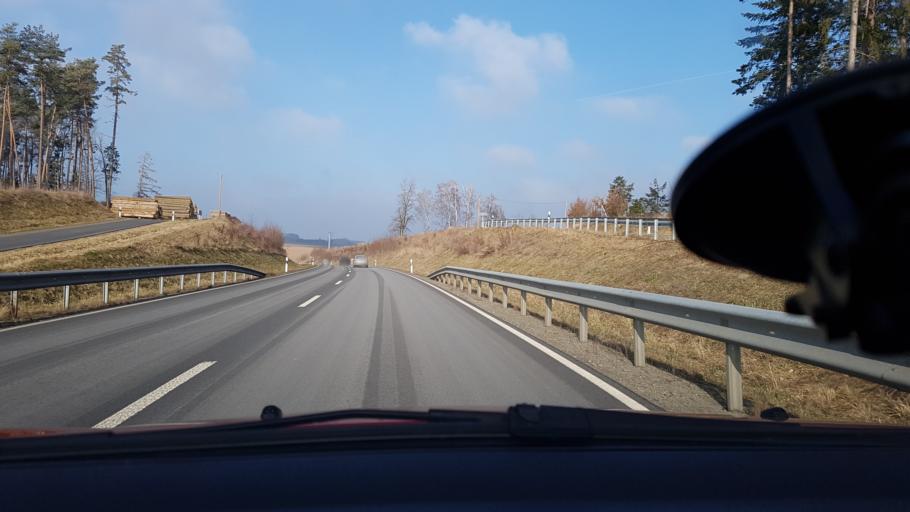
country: DE
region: Bavaria
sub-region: Lower Bavaria
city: Wittibreut
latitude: 48.3676
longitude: 12.9592
